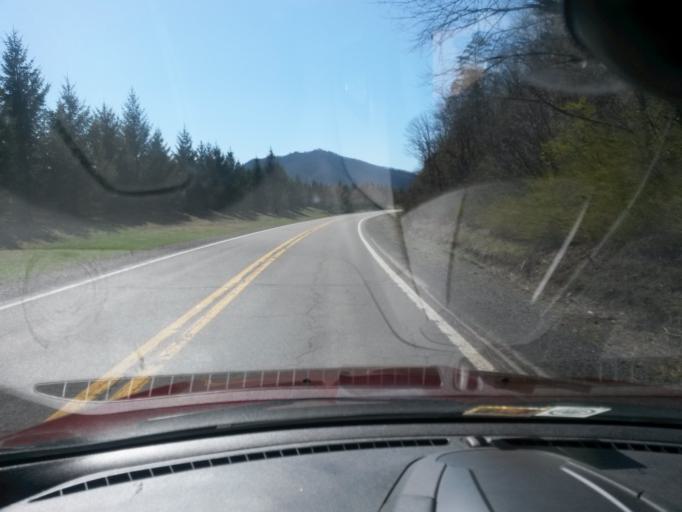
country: US
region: West Virginia
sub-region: Greenbrier County
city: White Sulphur Springs
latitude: 37.7775
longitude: -80.3286
